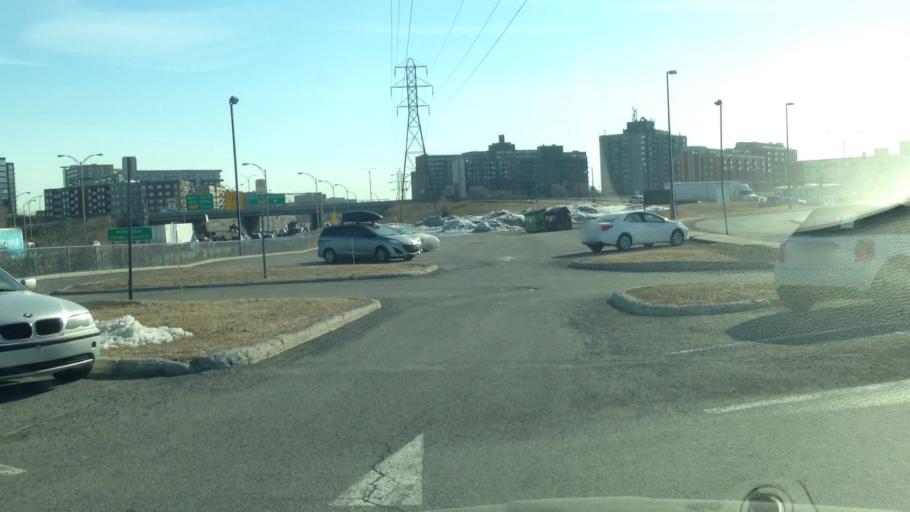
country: CA
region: Quebec
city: Saint-Laurent
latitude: 45.5298
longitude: -73.6864
